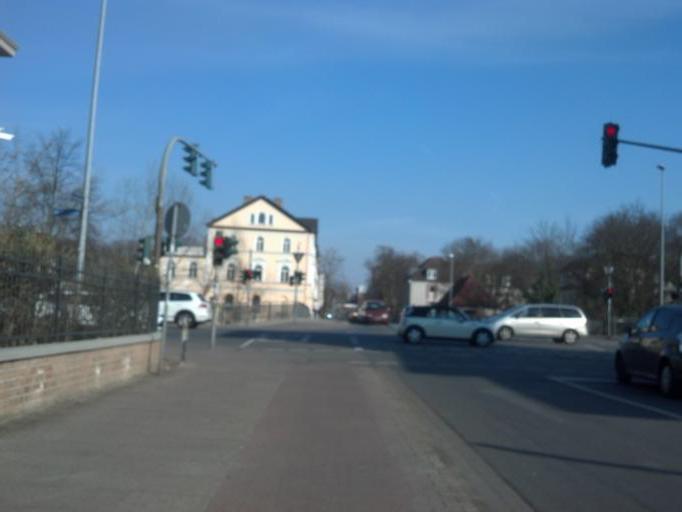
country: DE
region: Lower Saxony
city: Lueneburg
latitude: 53.2513
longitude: 10.4150
